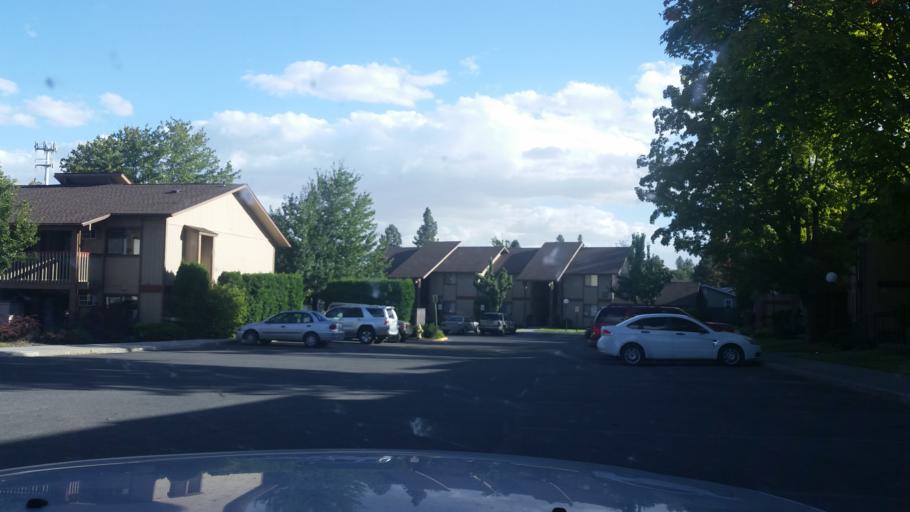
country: US
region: Washington
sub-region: Spokane County
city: Cheney
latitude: 47.5031
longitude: -117.5675
